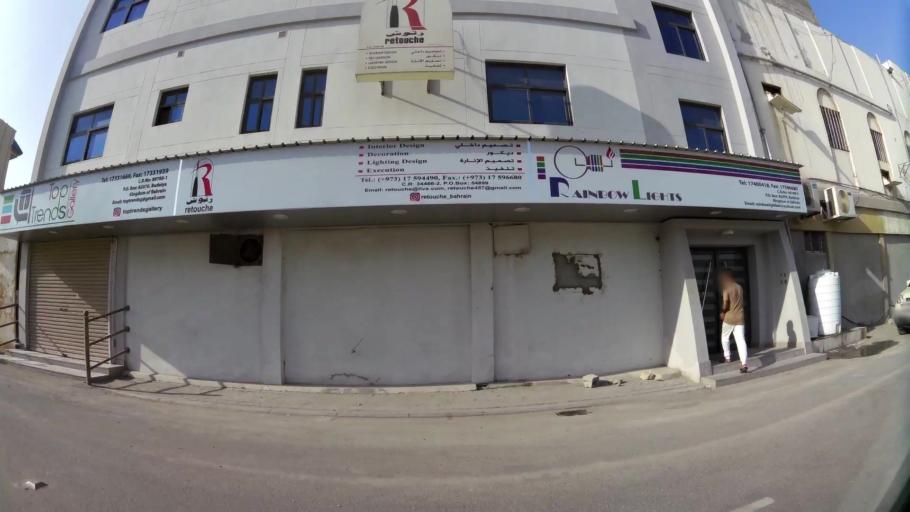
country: BH
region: Manama
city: Jidd Hafs
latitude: 26.2173
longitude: 50.5194
